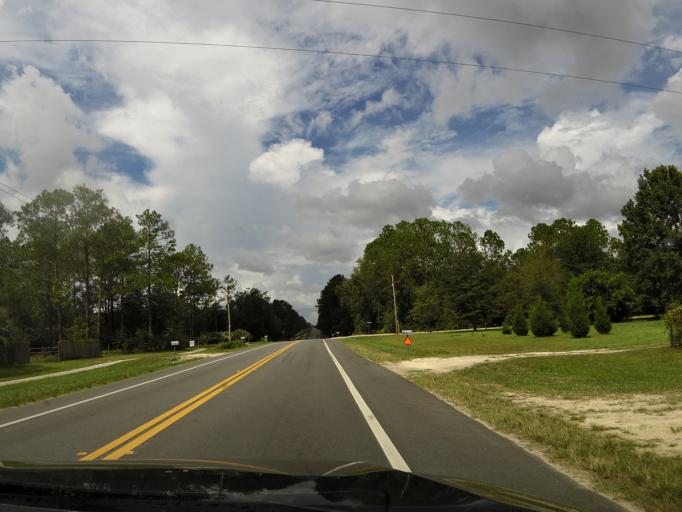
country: US
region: Florida
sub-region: Clay County
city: Middleburg
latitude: 30.0744
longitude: -81.9337
